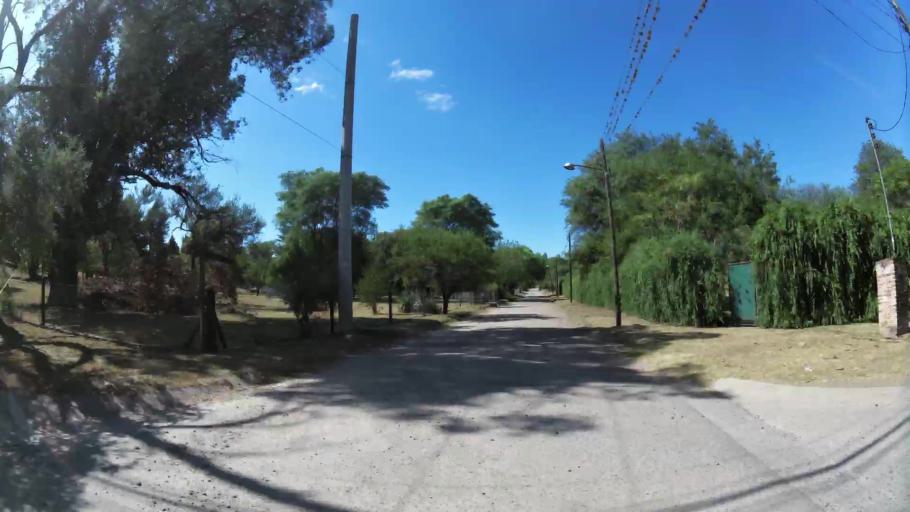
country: AR
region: Cordoba
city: Mendiolaza
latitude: -31.2753
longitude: -64.2921
